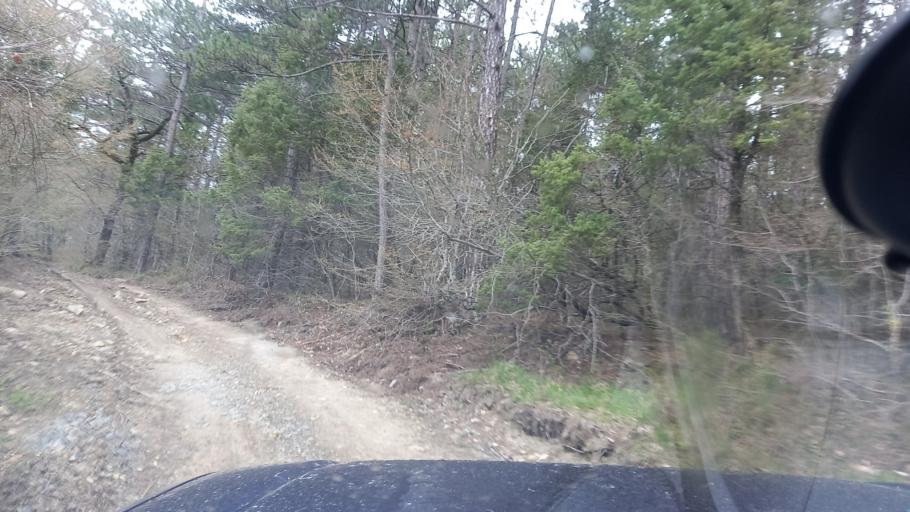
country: RU
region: Krasnodarskiy
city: Arkhipo-Osipovka
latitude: 44.3768
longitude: 38.4716
